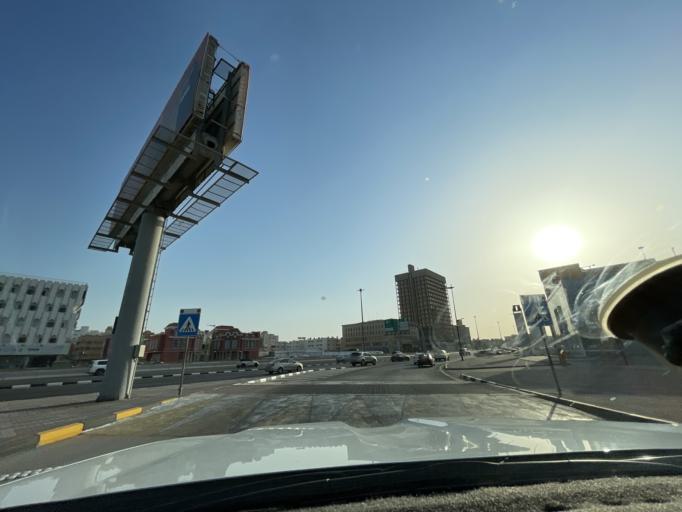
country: SA
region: Eastern Province
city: Khobar
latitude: 26.2829
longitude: 50.2028
